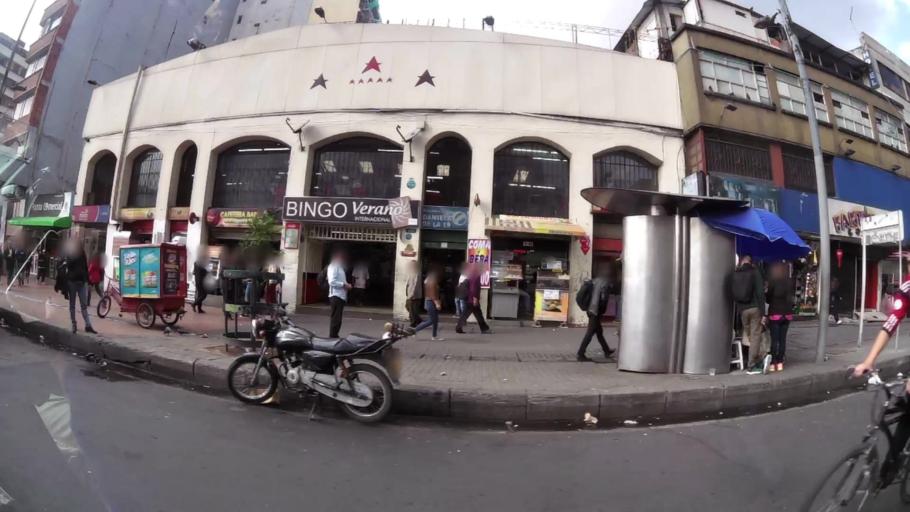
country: CO
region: Bogota D.C.
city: Bogota
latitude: 4.6065
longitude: -74.0735
